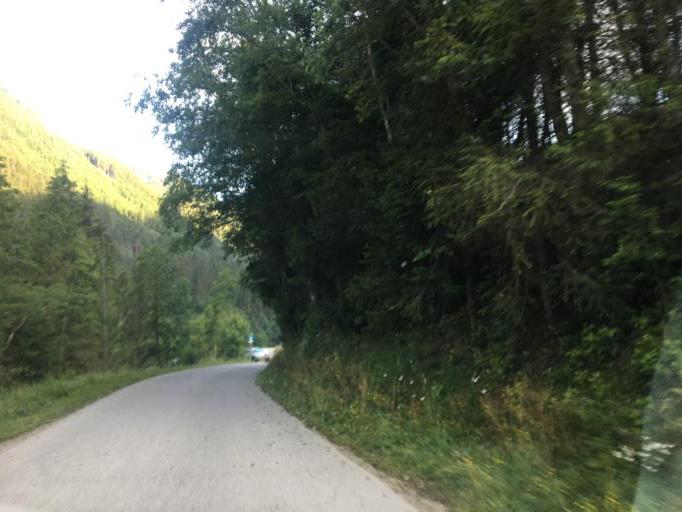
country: AT
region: Styria
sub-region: Politischer Bezirk Liezen
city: Haus
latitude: 47.3279
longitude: 13.7580
